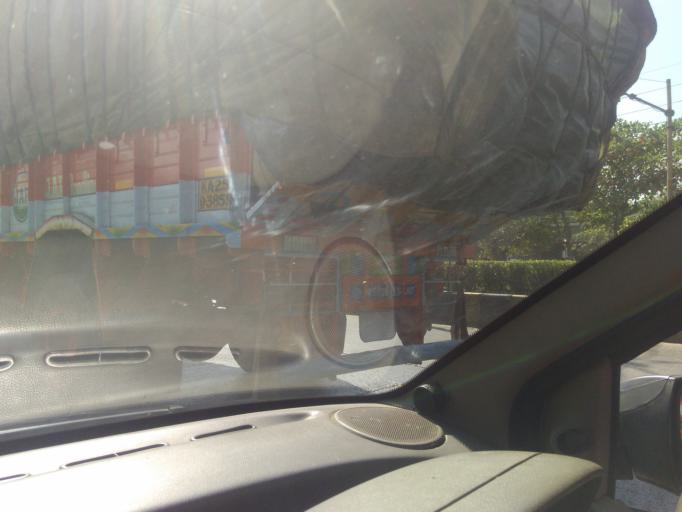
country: IN
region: Maharashtra
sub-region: Thane
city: Airoli
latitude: 19.1316
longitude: 73.0037
